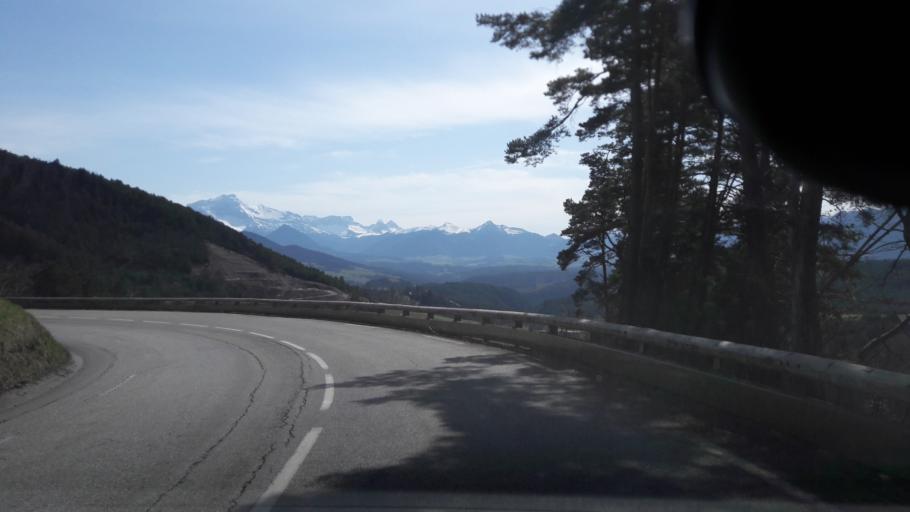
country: FR
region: Rhone-Alpes
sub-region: Departement de l'Isere
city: La Motte-Saint-Martin
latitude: 44.8977
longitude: 5.6304
